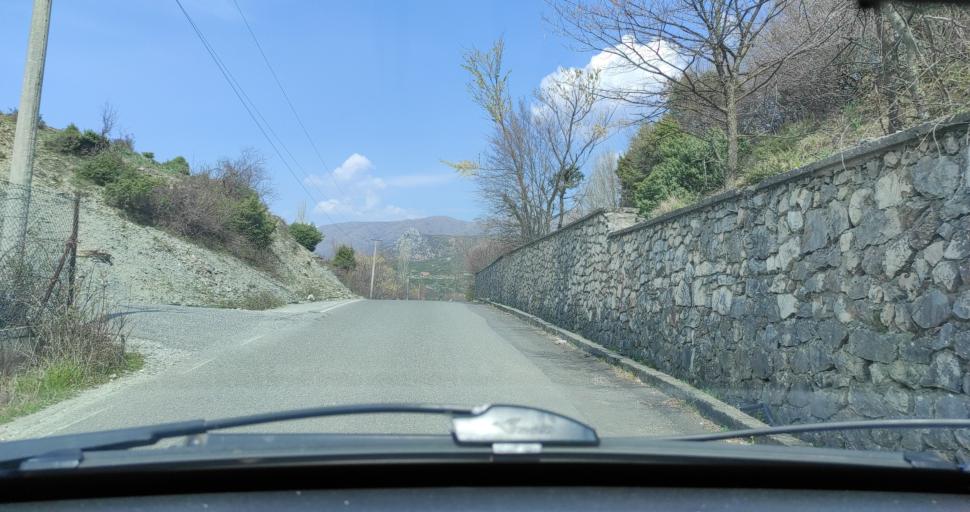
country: AL
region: Lezhe
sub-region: Rrethi i Lezhes
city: Kallmeti i Madh
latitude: 41.8631
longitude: 19.6986
